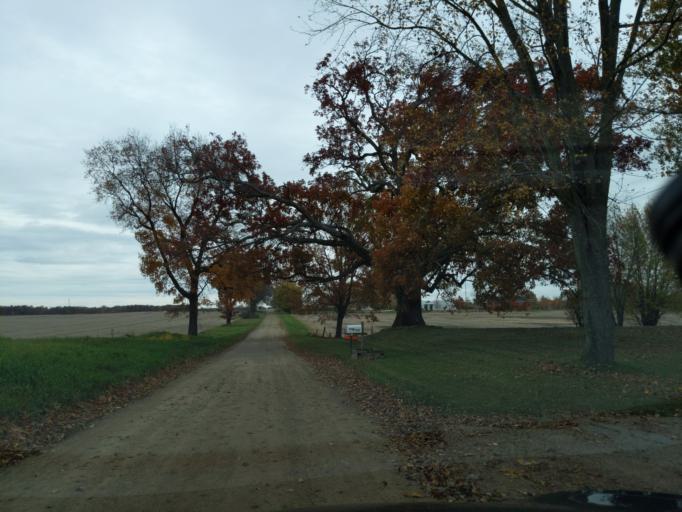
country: US
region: Michigan
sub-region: Eaton County
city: Eaton Rapids
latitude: 42.4329
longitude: -84.6005
